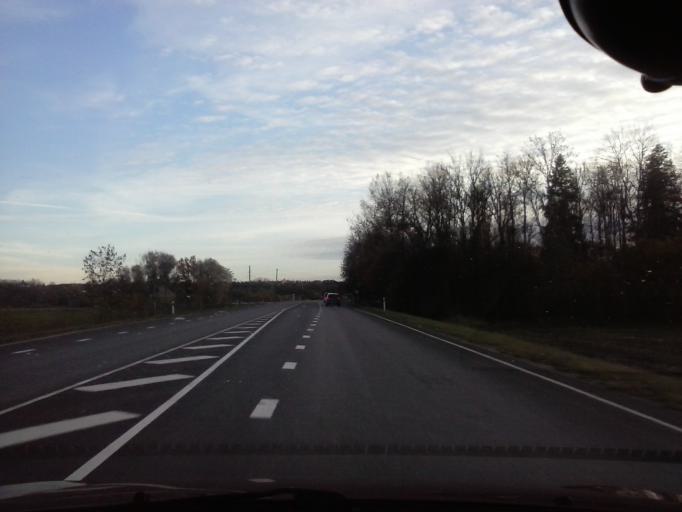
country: EE
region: Harju
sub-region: Nissi vald
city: Turba
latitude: 58.9054
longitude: 24.1101
